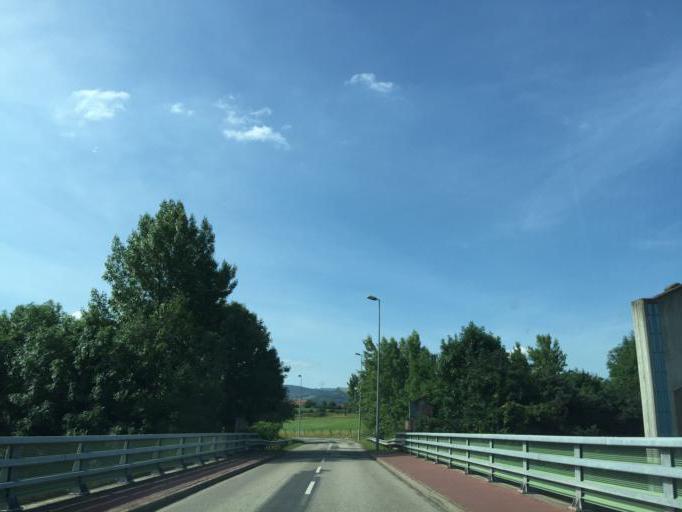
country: FR
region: Rhone-Alpes
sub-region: Departement de la Loire
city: La Grand-Croix
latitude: 45.4950
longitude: 4.5312
